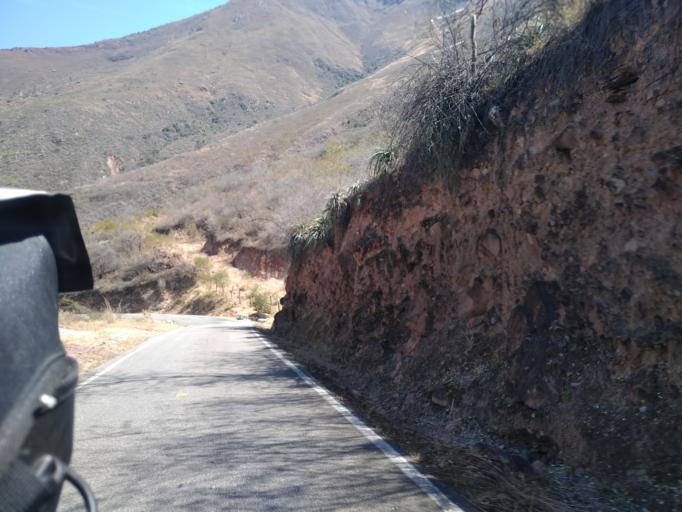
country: PE
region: Amazonas
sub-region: Provincia de Chachapoyas
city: Balsas
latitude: -6.8475
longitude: -77.9681
